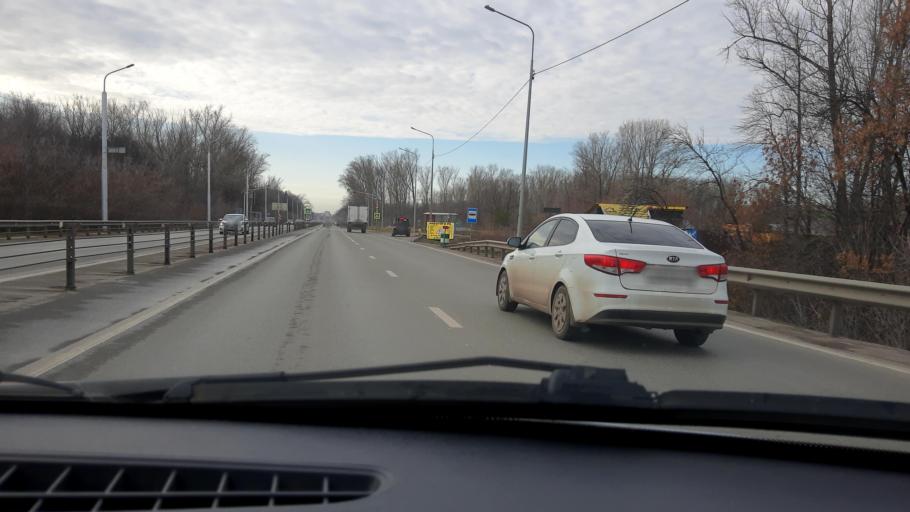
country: RU
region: Bashkortostan
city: Ufa
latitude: 54.7013
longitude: 55.9412
